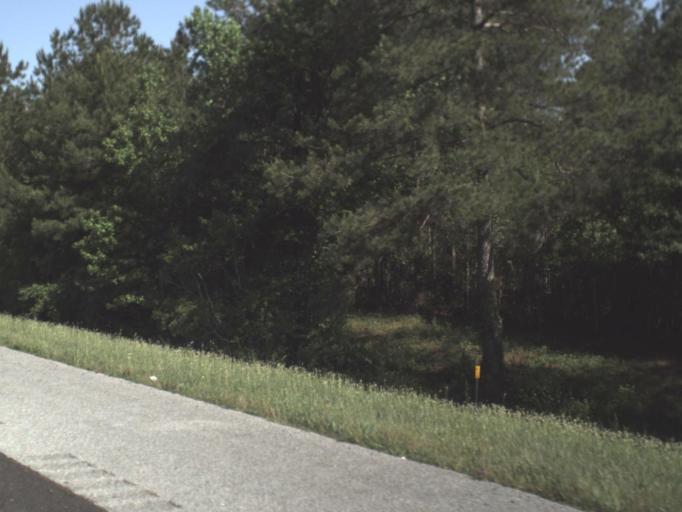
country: US
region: Florida
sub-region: Holmes County
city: Bonifay
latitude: 30.7585
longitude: -85.6419
